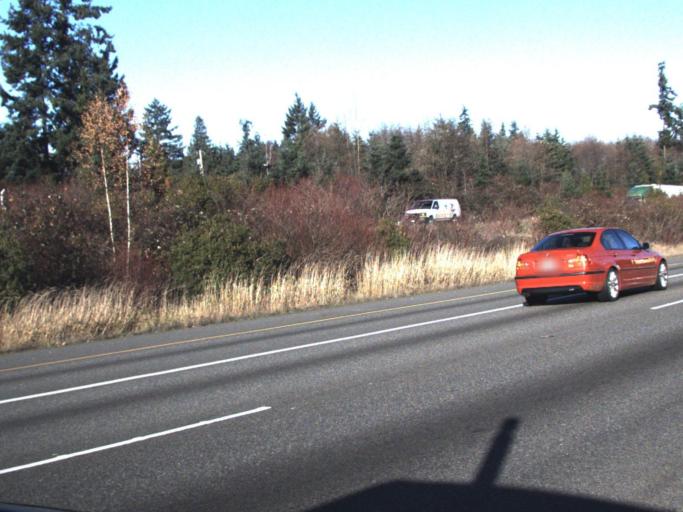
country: US
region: Washington
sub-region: Snohomish County
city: Martha Lake
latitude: 47.8702
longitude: -122.2443
